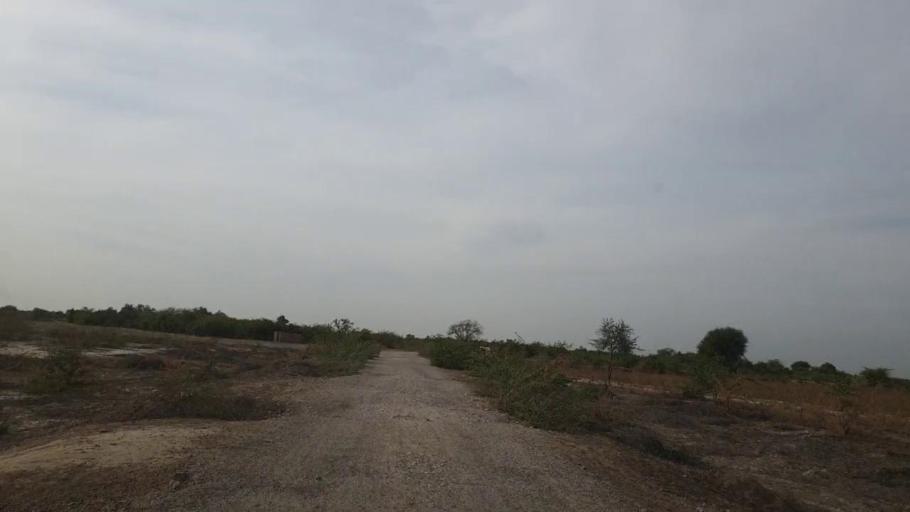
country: PK
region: Sindh
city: Nabisar
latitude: 24.9902
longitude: 69.5610
